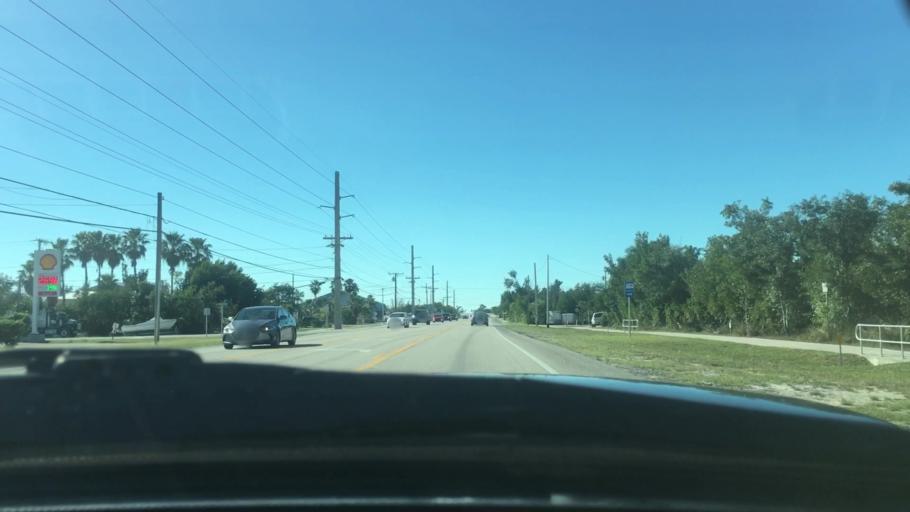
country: US
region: Florida
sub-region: Monroe County
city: Big Pine Key
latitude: 24.6700
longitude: -81.3644
